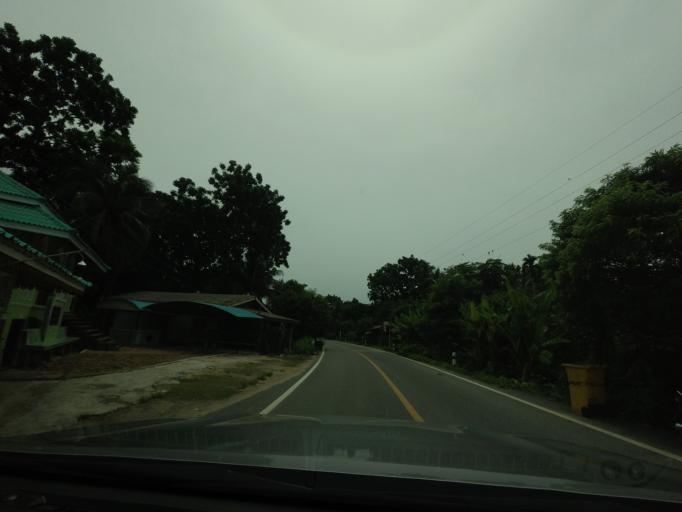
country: TH
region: Pattani
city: Kapho
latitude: 6.6083
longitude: 101.5385
